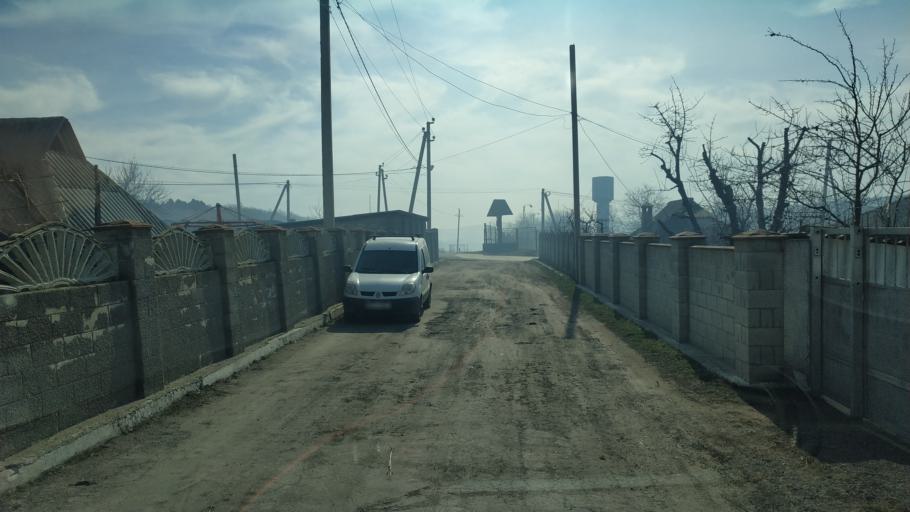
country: MD
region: Nisporeni
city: Nisporeni
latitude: 47.0736
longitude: 28.2647
